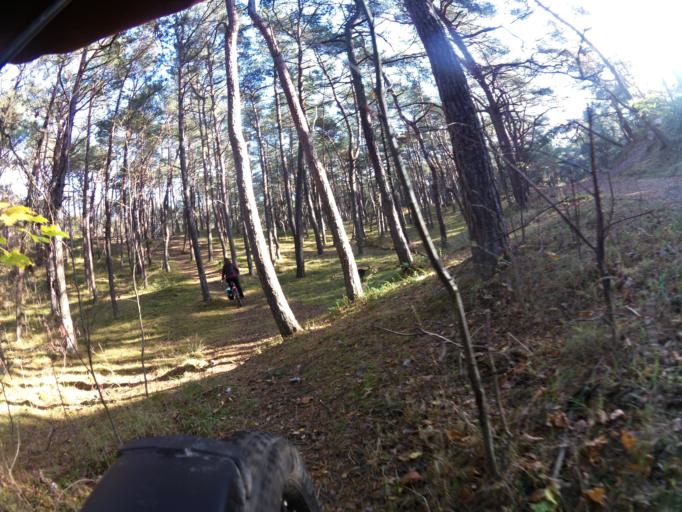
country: PL
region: Pomeranian Voivodeship
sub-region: Powiat pucki
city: Hel
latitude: 54.5987
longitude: 18.8128
